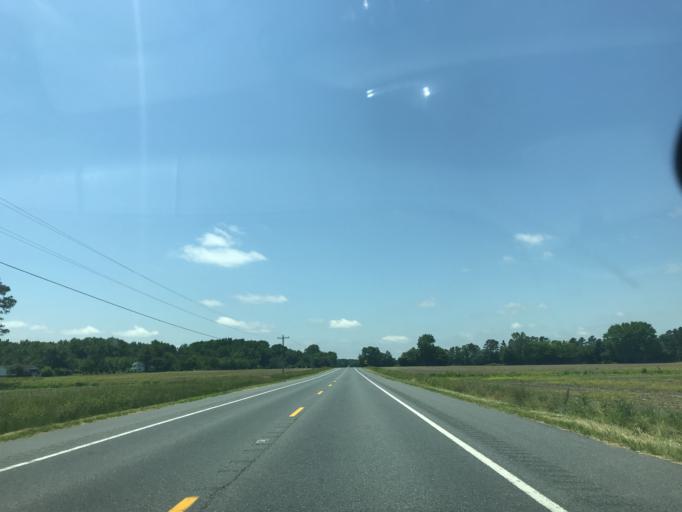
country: US
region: Maryland
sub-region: Caroline County
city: Federalsburg
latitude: 38.6306
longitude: -75.7319
